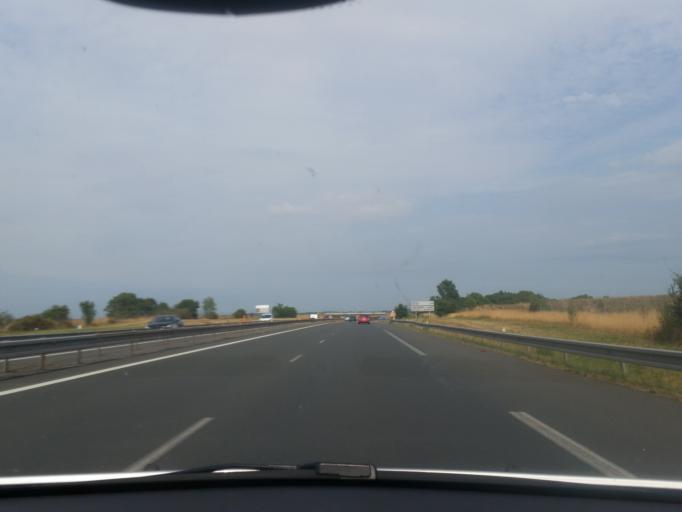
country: FR
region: Pays de la Loire
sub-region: Departement de la Loire-Atlantique
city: Ancenis
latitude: 47.4041
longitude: -1.1819
